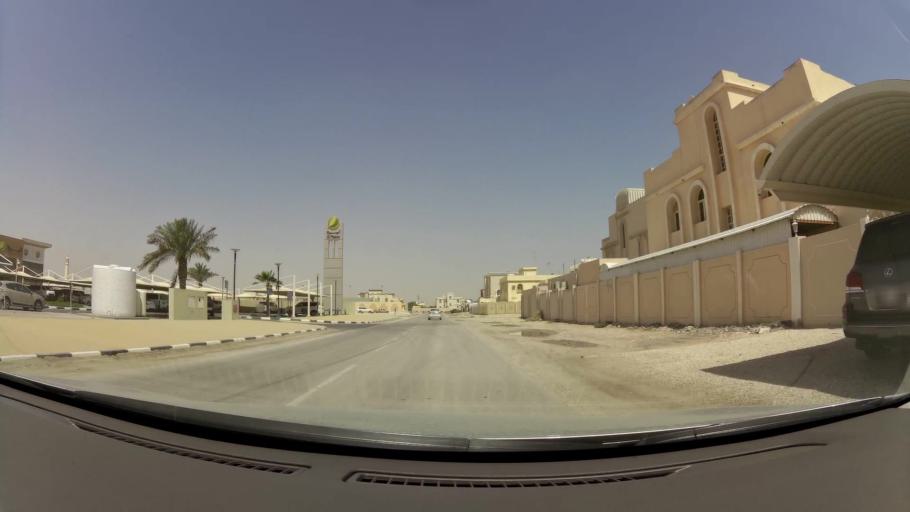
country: QA
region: Baladiyat Umm Salal
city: Umm Salal Muhammad
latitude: 25.3692
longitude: 51.4756
